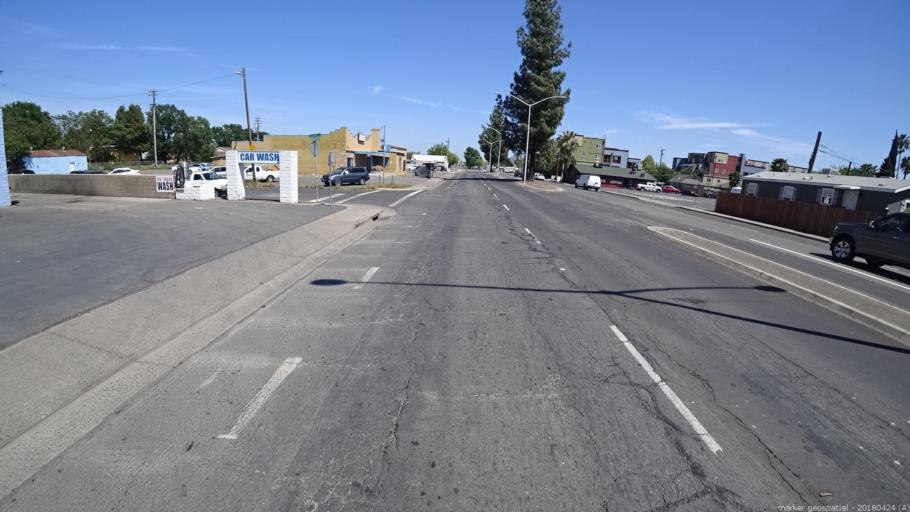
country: US
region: California
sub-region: Yolo County
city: West Sacramento
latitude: 38.5799
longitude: -121.5394
